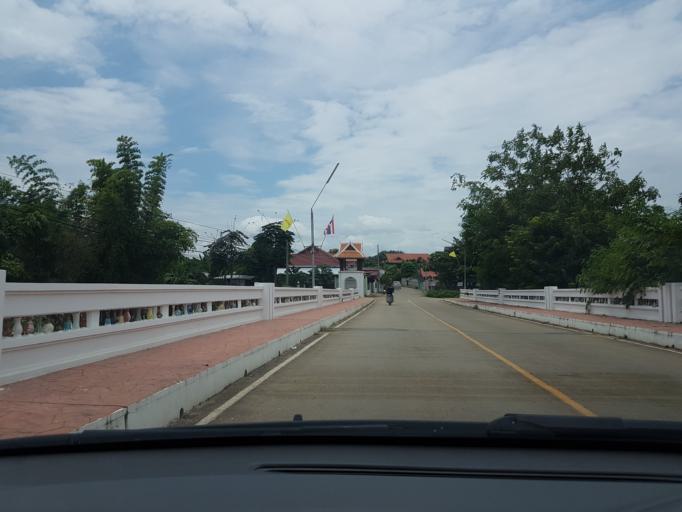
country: TH
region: Lampang
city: Ko Kha
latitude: 18.2178
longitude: 99.4149
